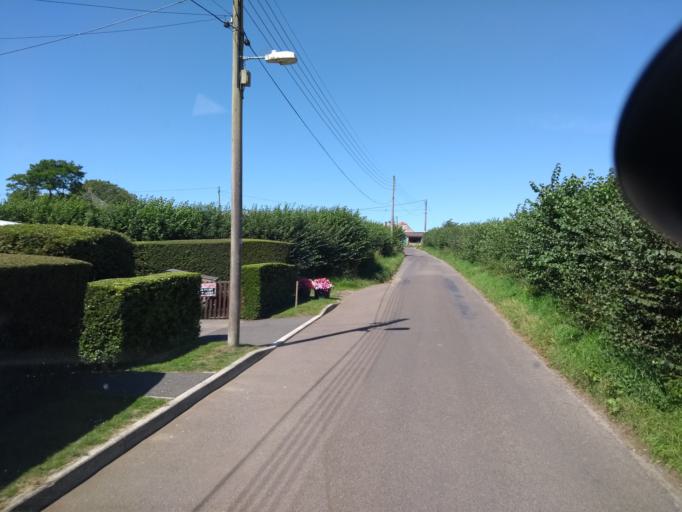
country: GB
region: England
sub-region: Somerset
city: Curry Rivel
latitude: 51.0277
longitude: -2.8672
